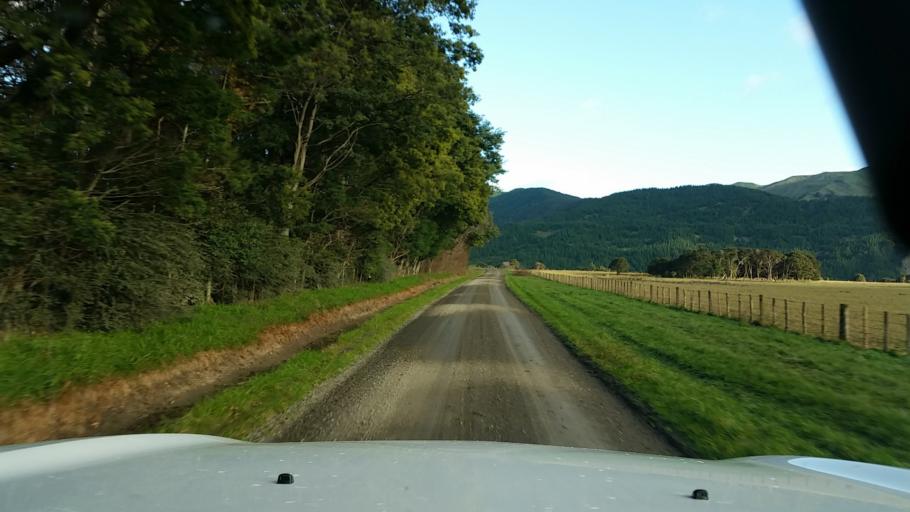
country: NZ
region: Wellington
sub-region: South Wairarapa District
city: Waipawa
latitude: -41.2647
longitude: 175.6800
